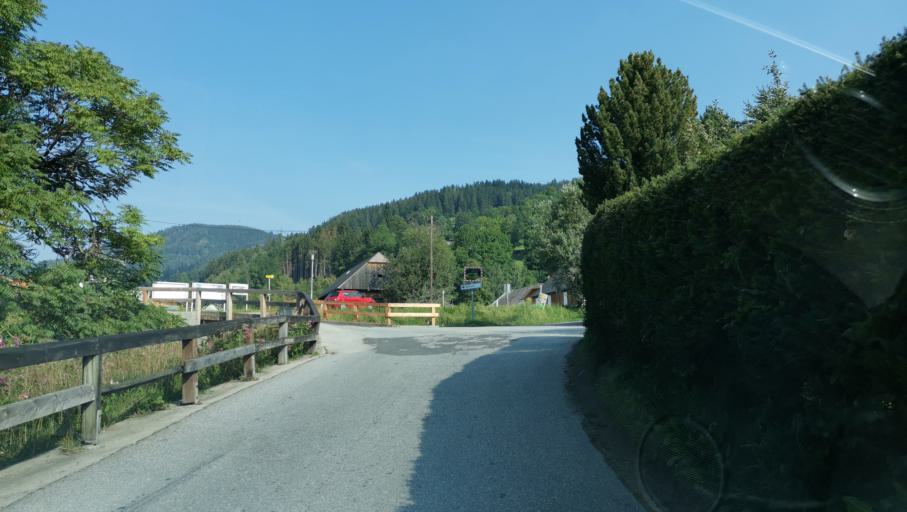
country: AT
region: Styria
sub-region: Politischer Bezirk Liezen
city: Trieben
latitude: 47.5028
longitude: 14.4770
